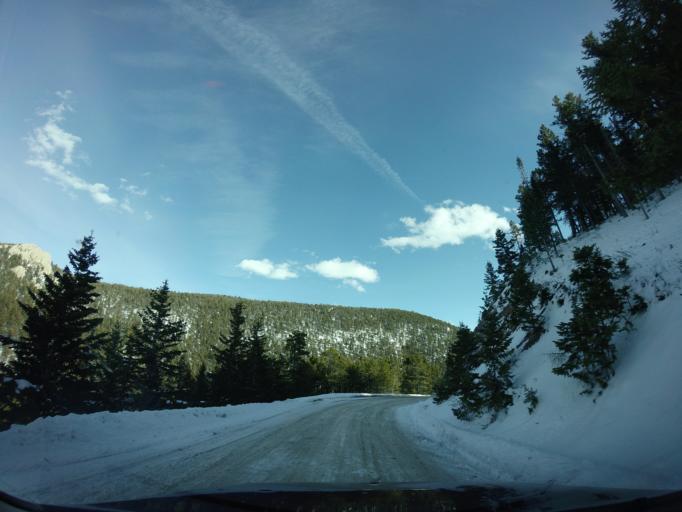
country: US
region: Montana
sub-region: Carbon County
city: Red Lodge
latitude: 45.1786
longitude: -109.3196
